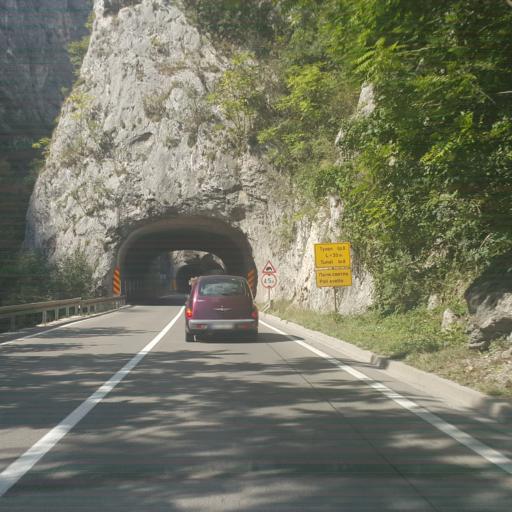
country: RS
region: Central Serbia
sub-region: Nisavski Okrug
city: Svrljig
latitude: 43.3267
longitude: 22.1624
